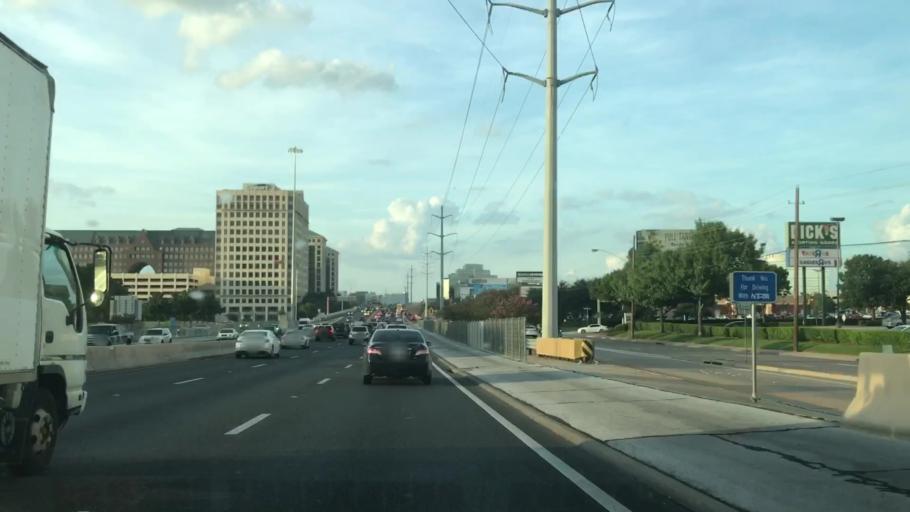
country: US
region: Texas
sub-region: Dallas County
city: Addison
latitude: 32.9350
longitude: -96.8219
